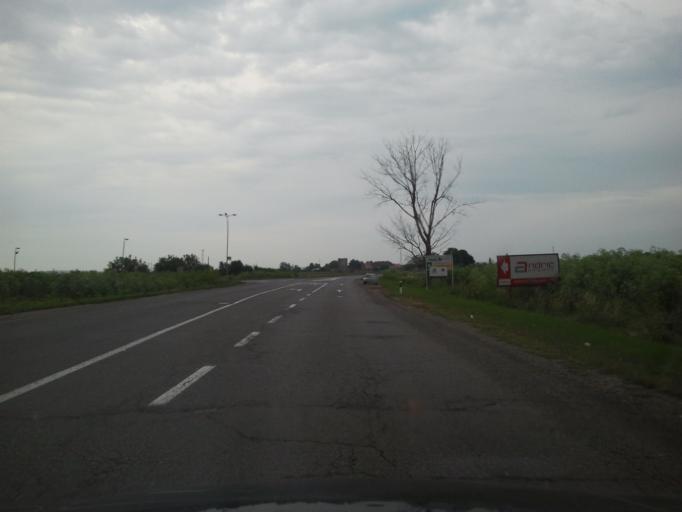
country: RS
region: Autonomna Pokrajina Vojvodina
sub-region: Sremski Okrug
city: Ruma
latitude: 44.9827
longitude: 19.8183
